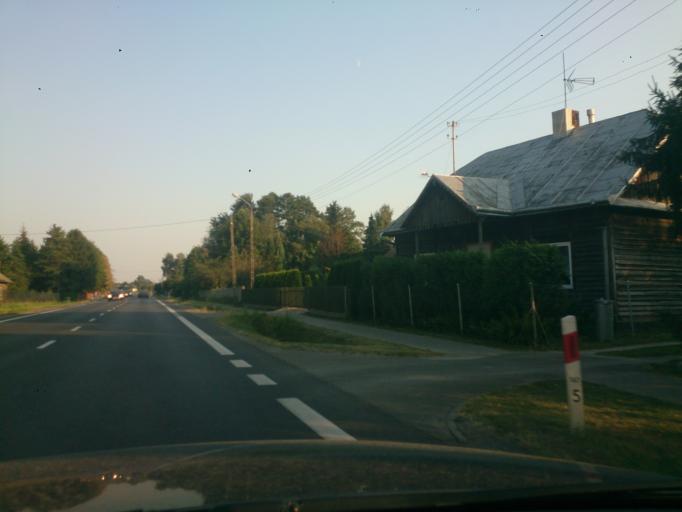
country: PL
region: Subcarpathian Voivodeship
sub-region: Powiat kolbuszowski
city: Kolbuszowa
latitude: 50.2312
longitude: 21.7885
